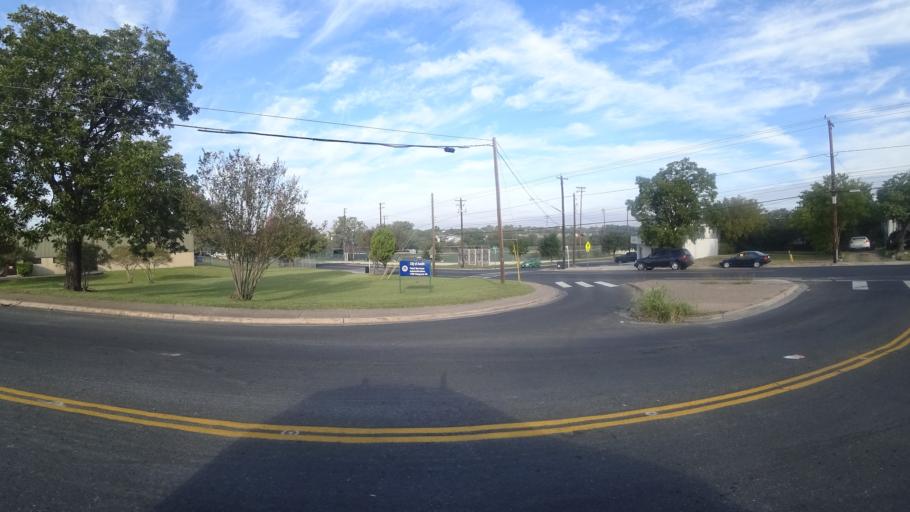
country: US
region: Texas
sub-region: Travis County
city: Austin
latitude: 30.2754
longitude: -97.7078
